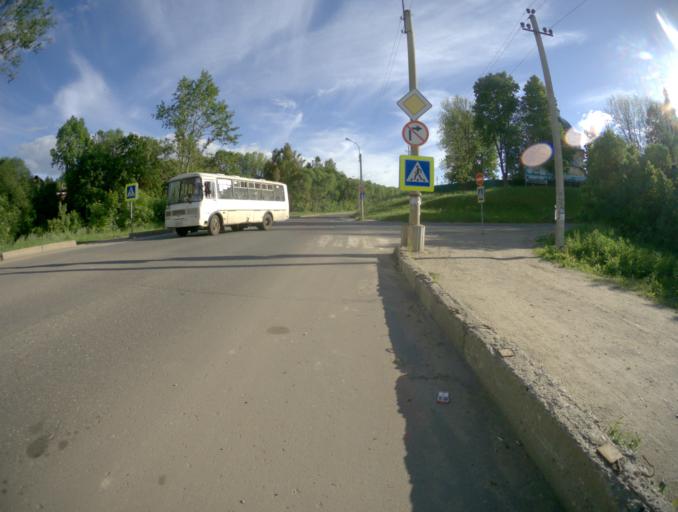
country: RU
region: Ivanovo
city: Lezhnevo
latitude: 56.7759
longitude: 40.8912
